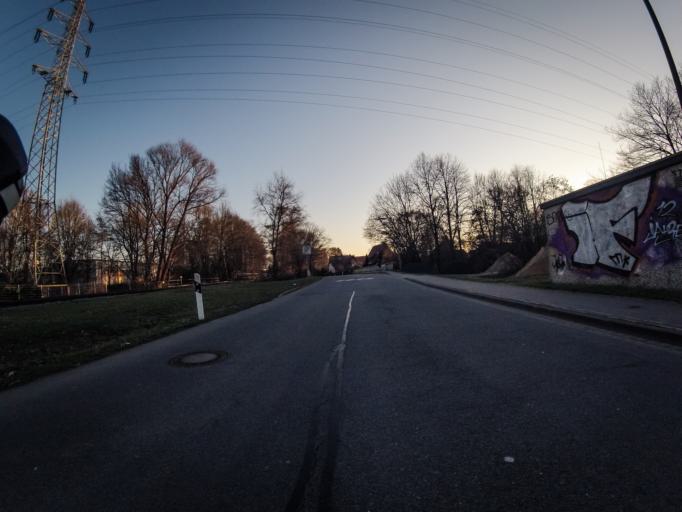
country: DE
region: Lower Saxony
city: Wallenhorst
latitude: 52.3087
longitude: 8.0007
